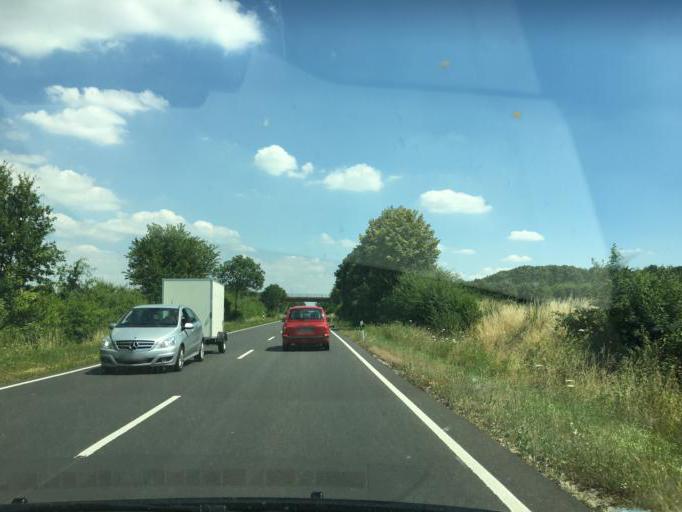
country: DE
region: North Rhine-Westphalia
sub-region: Regierungsbezirk Koln
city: Langerwehe
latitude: 50.8263
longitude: 6.3387
